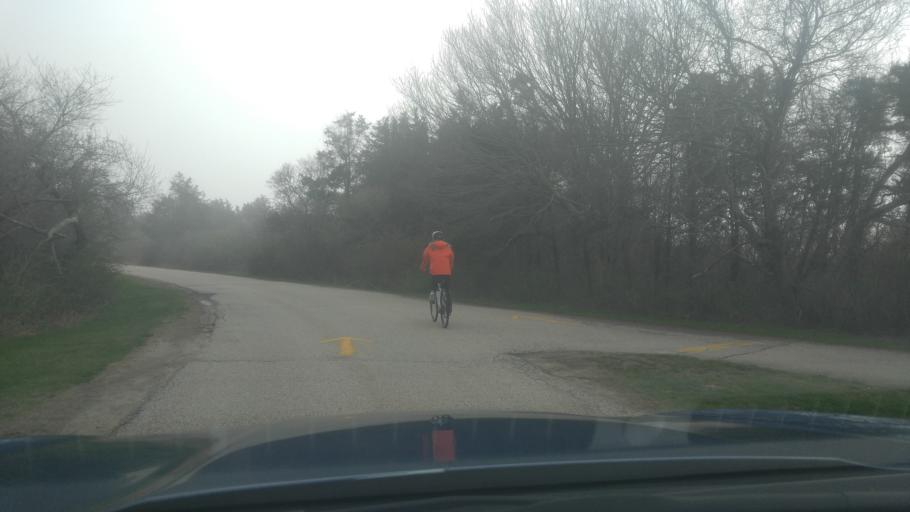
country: US
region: Rhode Island
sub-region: Newport County
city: Jamestown
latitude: 41.4555
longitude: -71.3990
